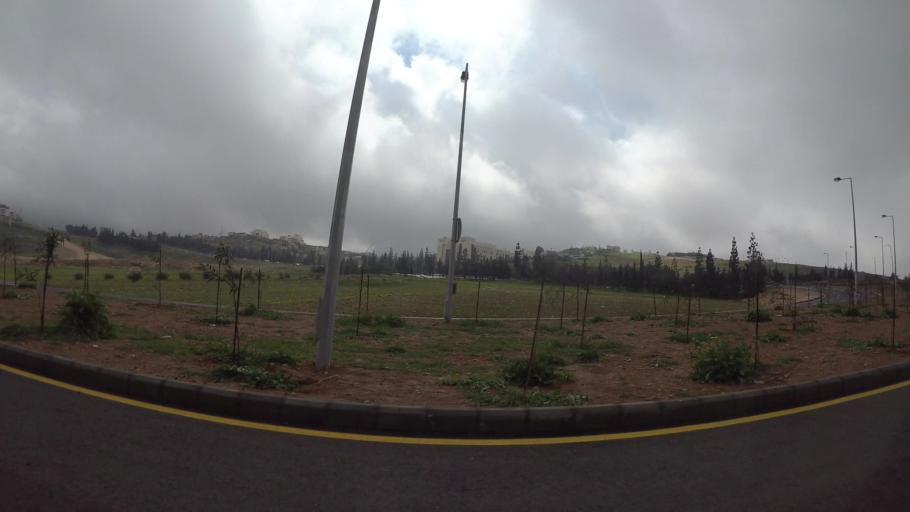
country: JO
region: Amman
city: Wadi as Sir
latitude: 31.9364
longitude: 35.8563
